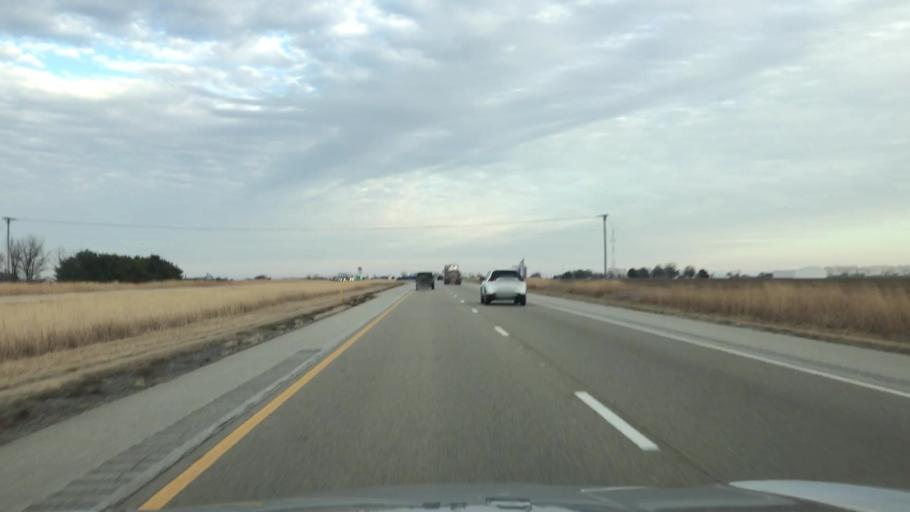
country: US
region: Illinois
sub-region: Logan County
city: Lincoln
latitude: 40.1816
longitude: -89.3504
